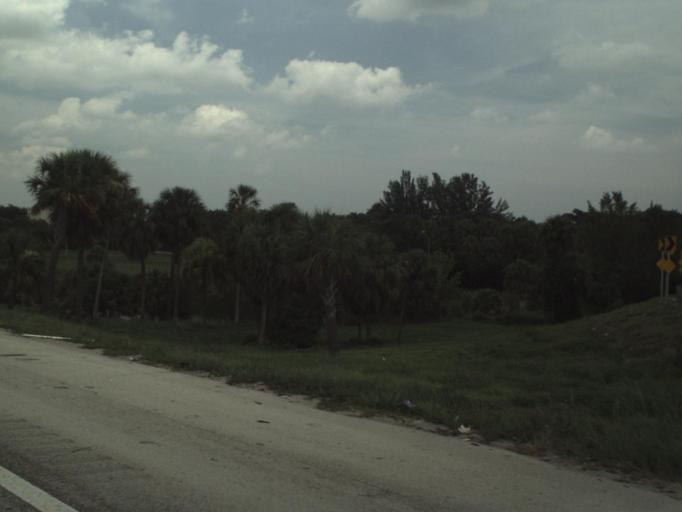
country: US
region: Florida
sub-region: Broward County
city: Deerfield Beach
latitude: 26.3198
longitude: -80.1161
